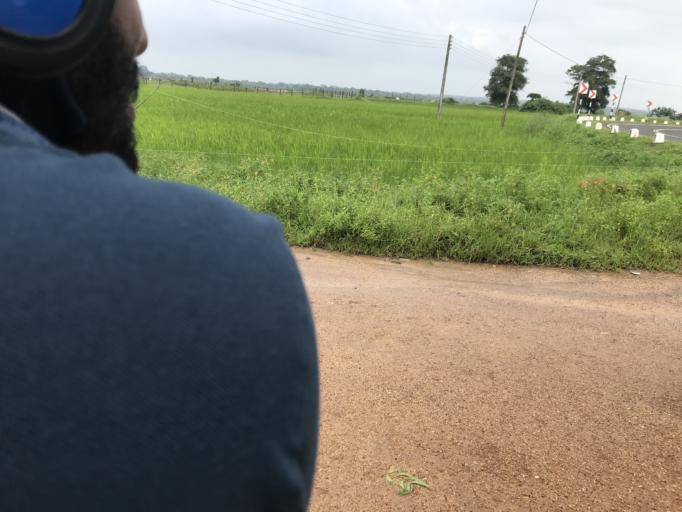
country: LK
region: Uva
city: Wattegama
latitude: 6.9216
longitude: 81.8251
